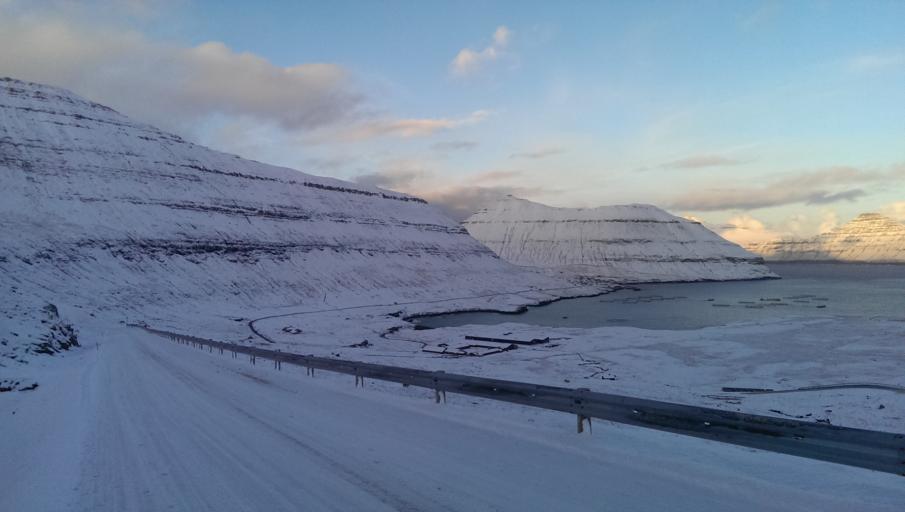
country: FO
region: Eysturoy
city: Fuglafjordur
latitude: 62.2518
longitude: -6.8609
